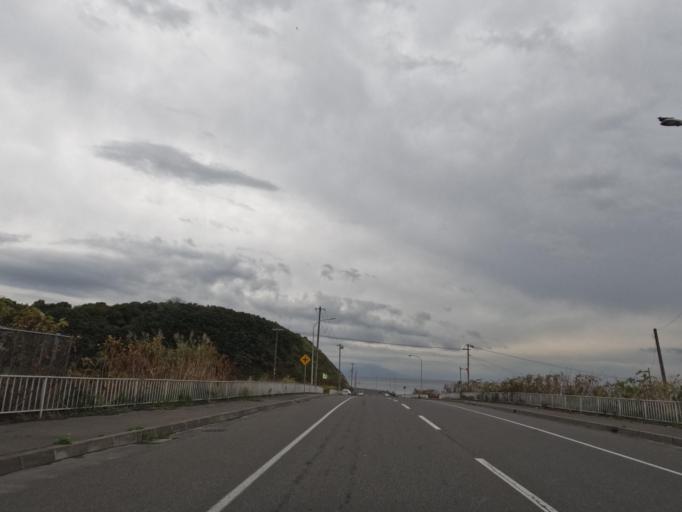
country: JP
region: Hokkaido
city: Date
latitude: 42.3810
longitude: 140.9101
